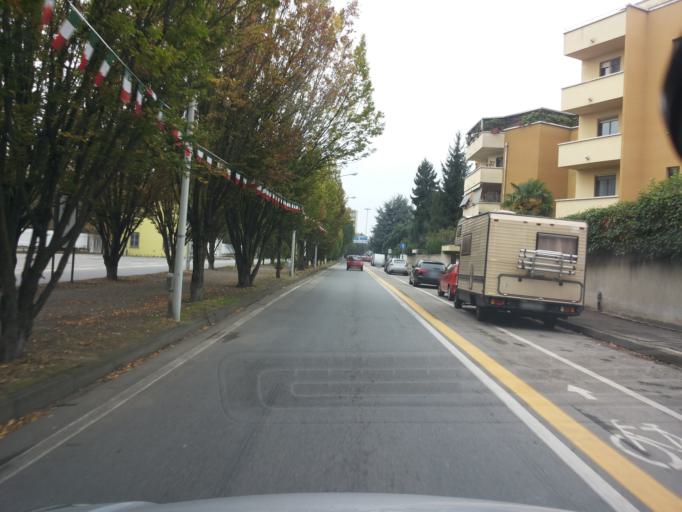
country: IT
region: Piedmont
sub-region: Provincia di Vercelli
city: Vercelli
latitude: 45.3162
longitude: 8.4294
